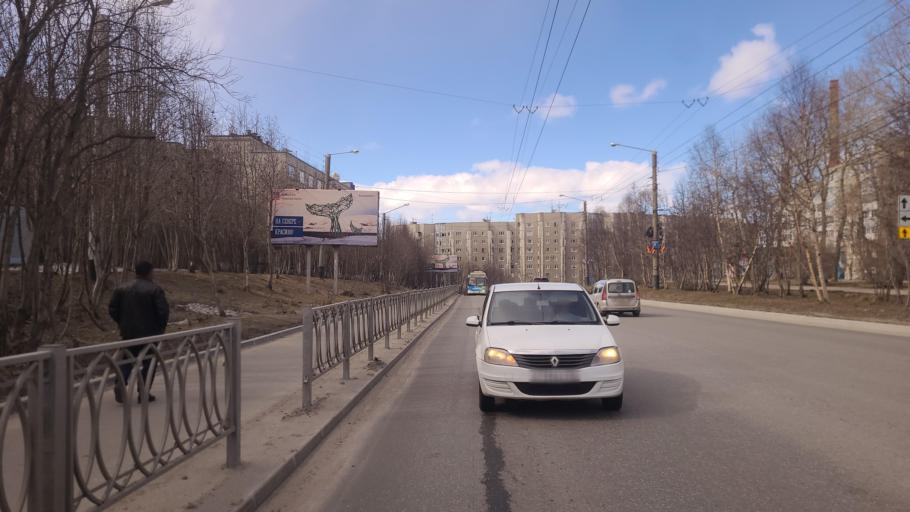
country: RU
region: Murmansk
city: Murmansk
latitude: 68.9540
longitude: 33.0659
